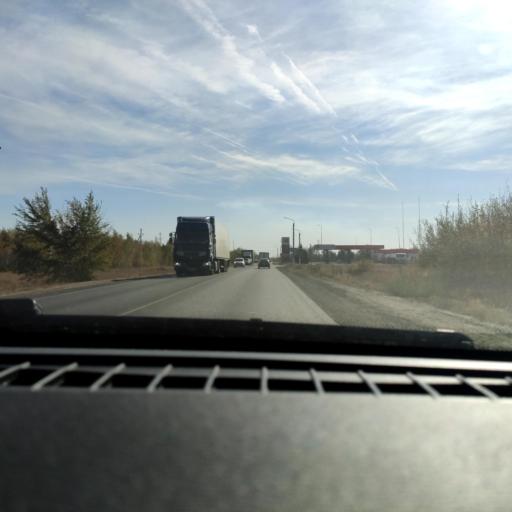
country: RU
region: Voronezj
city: Maslovka
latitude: 51.5880
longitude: 39.2532
